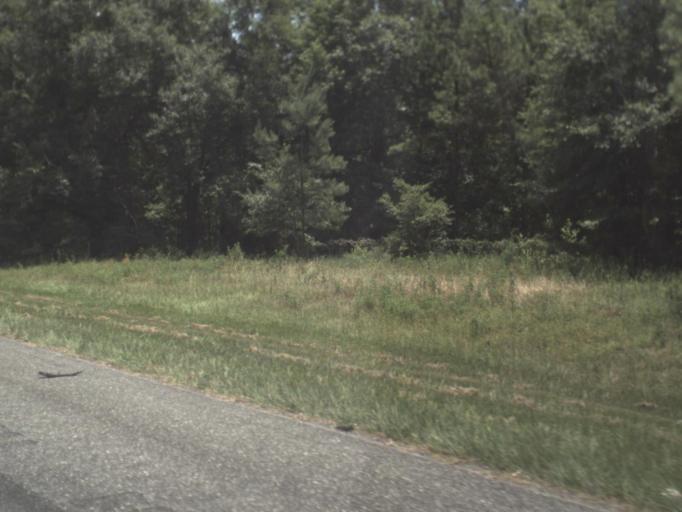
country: US
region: Florida
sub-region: Madison County
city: Madison
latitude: 30.4301
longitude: -83.5672
